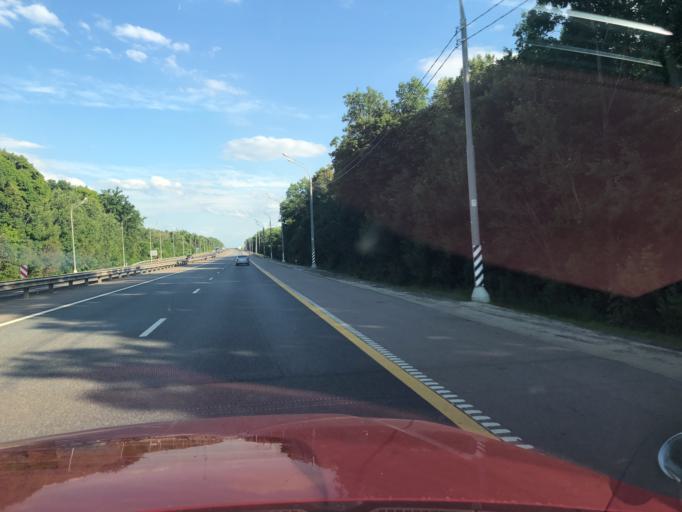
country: RU
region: Lipetsk
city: Zadonsk
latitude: 52.4206
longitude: 38.8361
